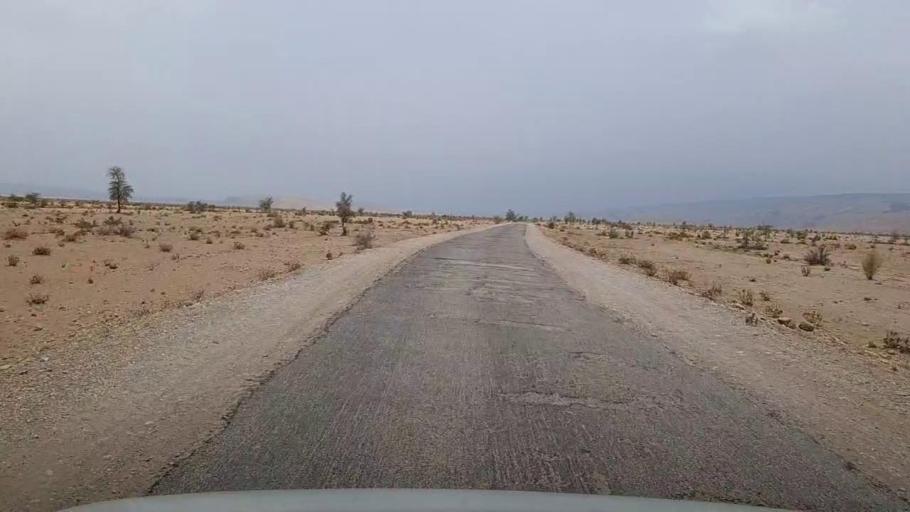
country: PK
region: Sindh
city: Sehwan
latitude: 26.2689
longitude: 67.7237
